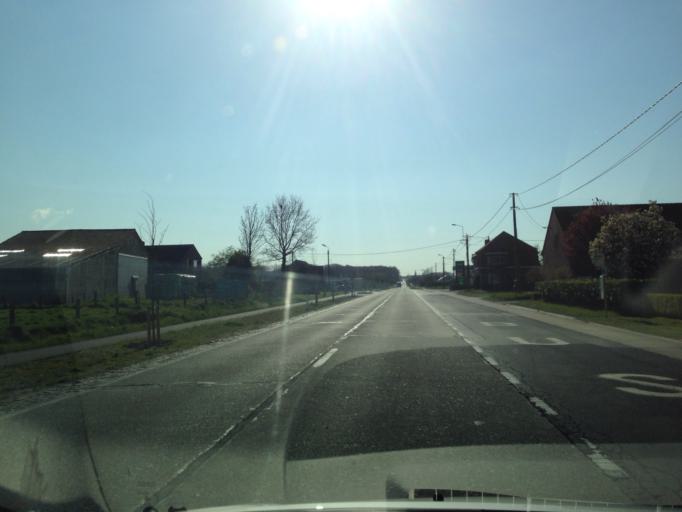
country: BE
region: Flanders
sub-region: Provincie West-Vlaanderen
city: Zedelgem
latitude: 51.1256
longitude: 3.1297
